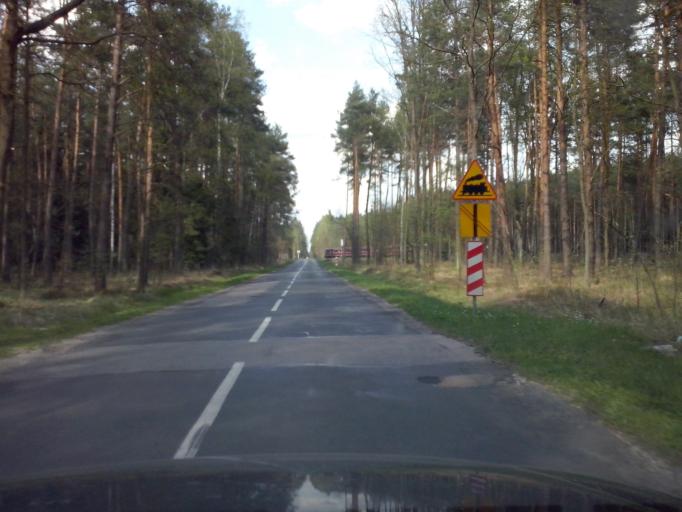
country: PL
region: Subcarpathian Voivodeship
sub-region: Powiat lezajski
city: Letownia
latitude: 50.3709
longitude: 22.2504
